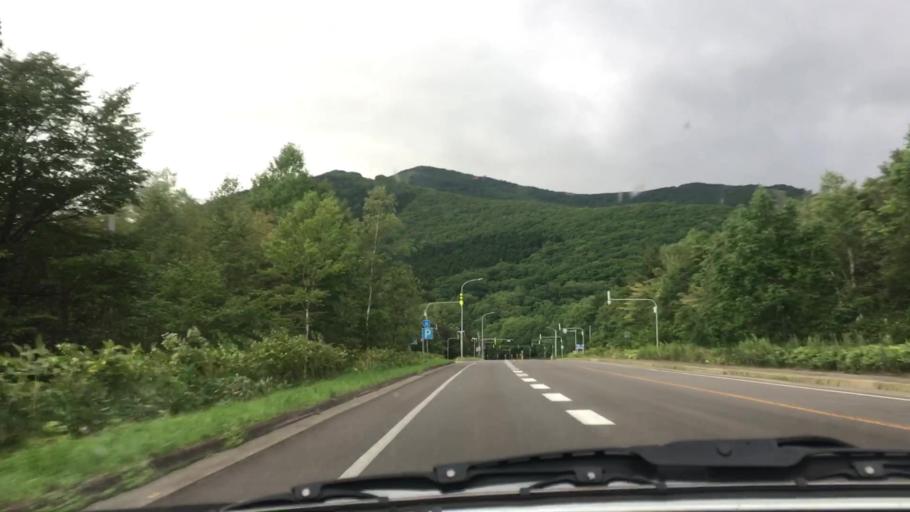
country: JP
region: Hokkaido
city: Otofuke
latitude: 43.1632
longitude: 142.8101
